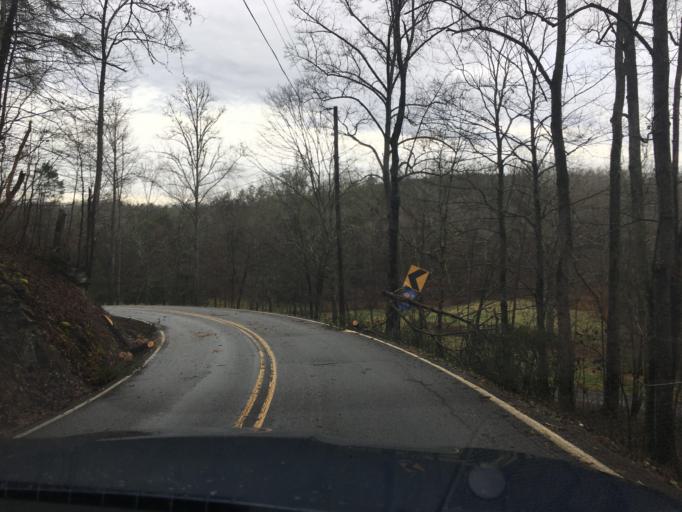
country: US
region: Tennessee
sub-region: McMinn County
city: Englewood
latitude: 35.3639
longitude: -84.4258
